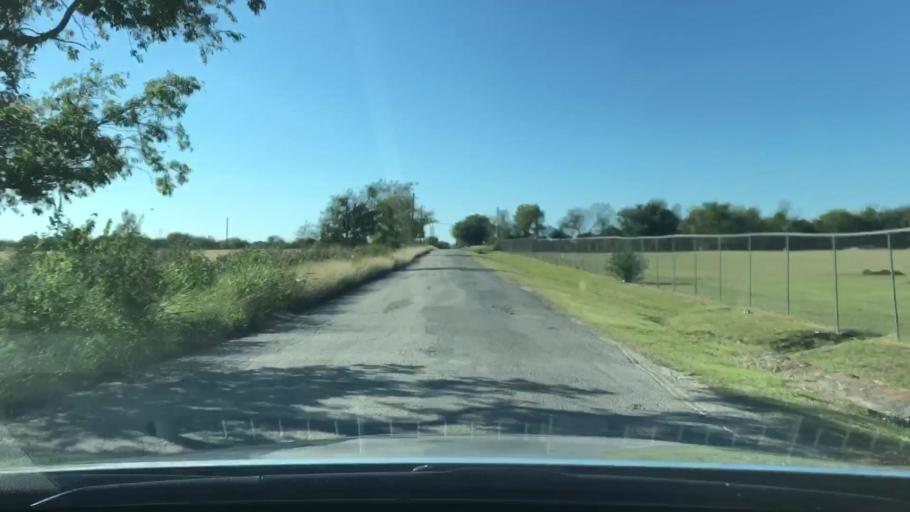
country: US
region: Texas
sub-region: Bexar County
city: Converse
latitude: 29.4667
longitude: -98.2975
